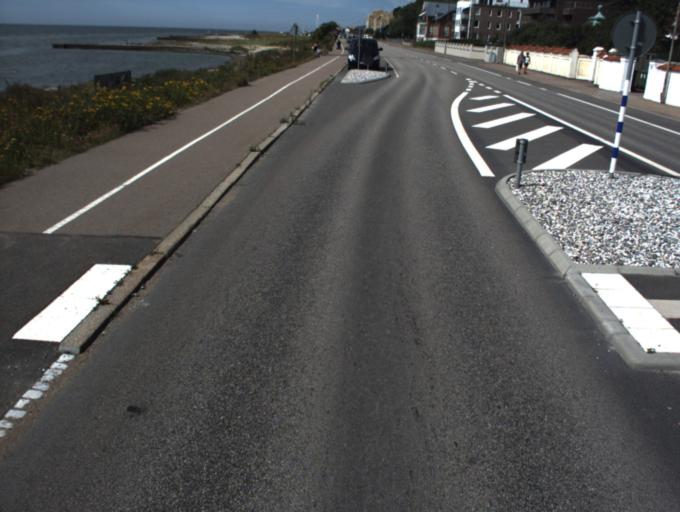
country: SE
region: Skane
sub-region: Helsingborg
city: Helsingborg
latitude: 56.0683
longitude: 12.6742
